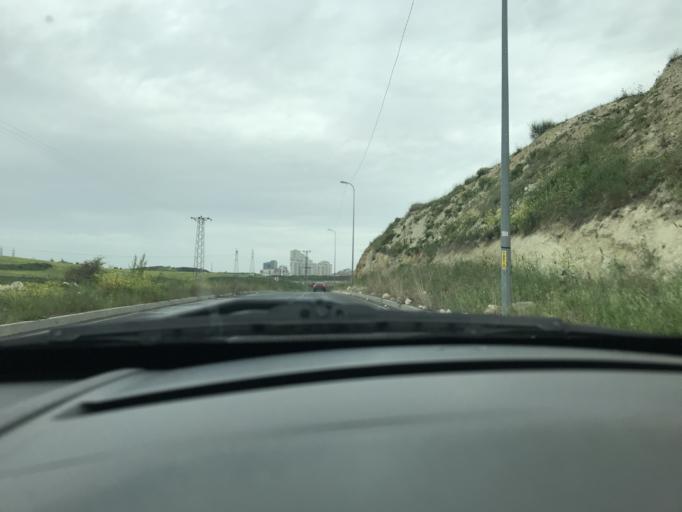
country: TR
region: Istanbul
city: Esenyurt
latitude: 41.0929
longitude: 28.6809
